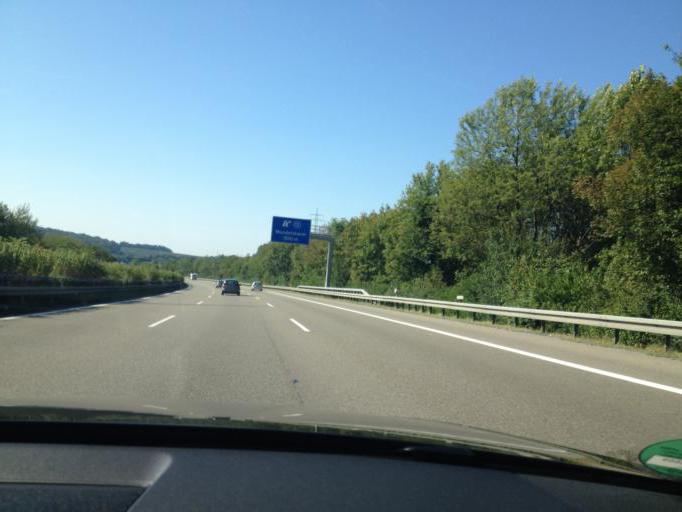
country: DE
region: Baden-Wuerttemberg
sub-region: Regierungsbezirk Stuttgart
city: Ilsfeld
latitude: 49.0221
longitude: 9.2487
